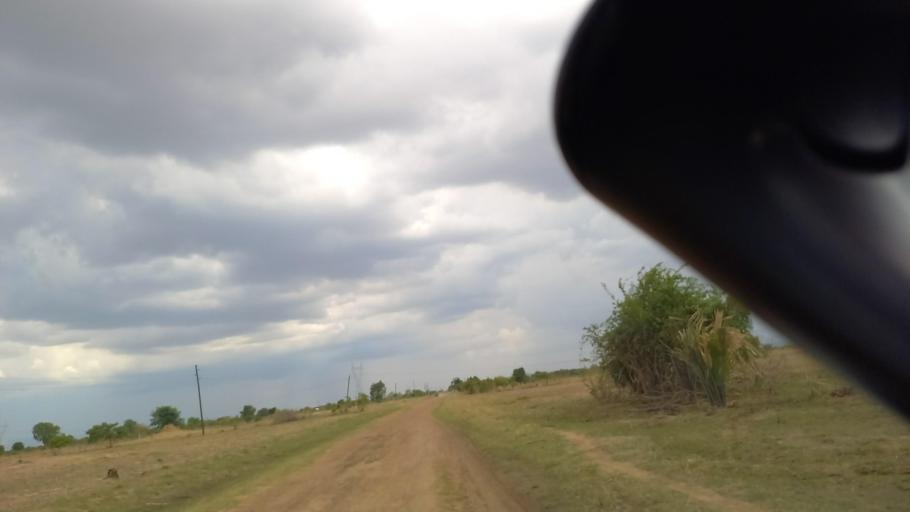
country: ZM
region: Lusaka
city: Kafue
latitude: -15.8460
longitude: 28.0995
